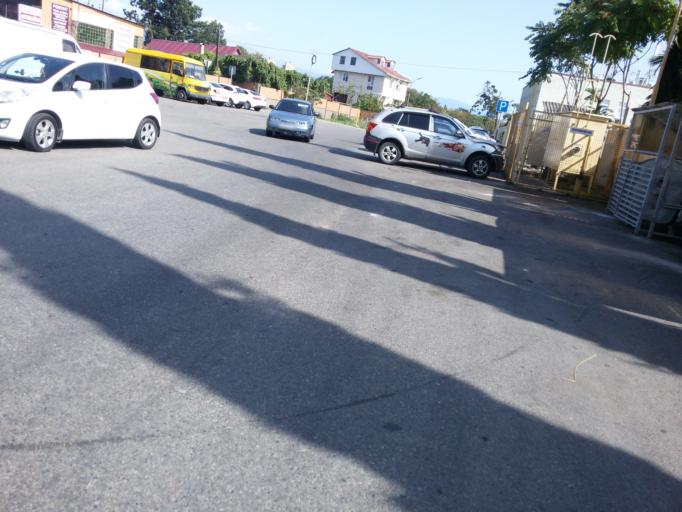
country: RU
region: Krasnodarskiy
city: Adler
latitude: 43.4186
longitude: 39.9385
